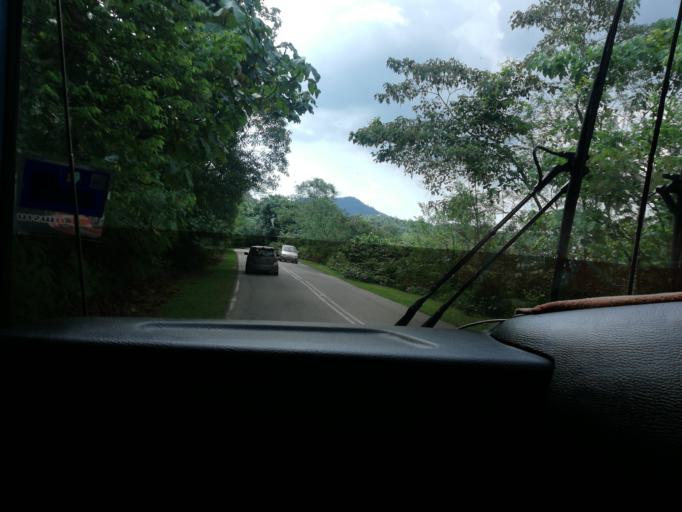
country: MY
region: Kedah
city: Kulim
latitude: 5.3194
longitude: 100.5975
